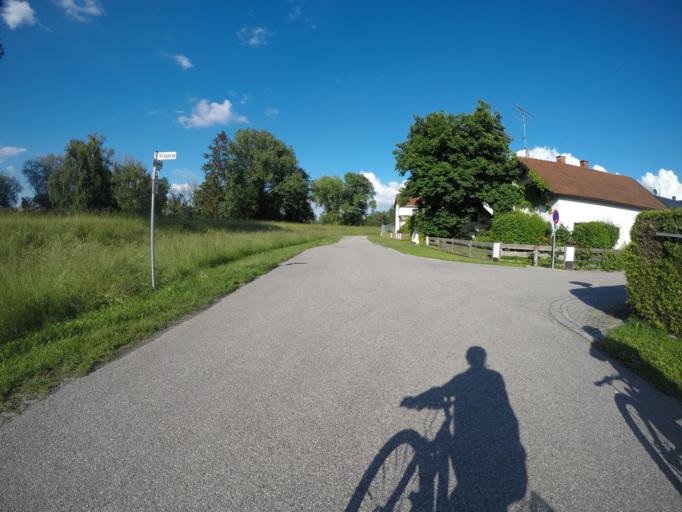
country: DE
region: Bavaria
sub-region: Lower Bavaria
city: Marklkofen
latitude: 48.5570
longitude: 12.5560
